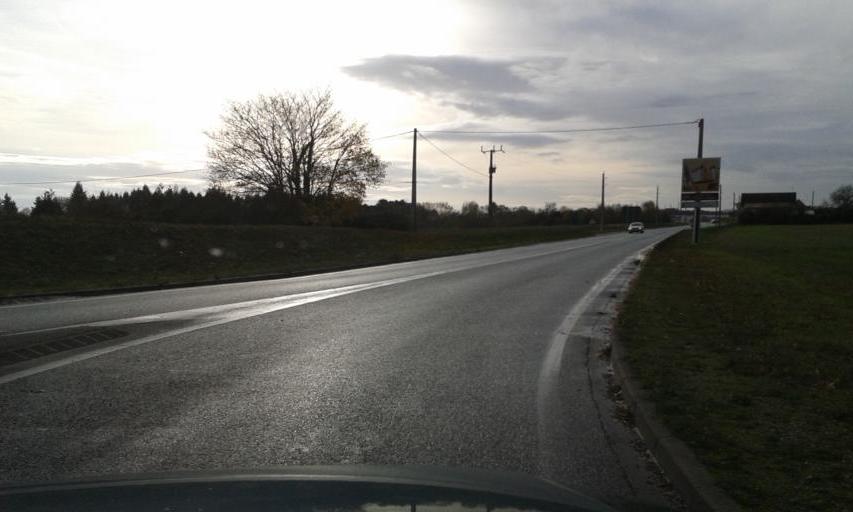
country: FR
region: Centre
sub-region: Departement du Loiret
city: Saint-Ay
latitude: 47.8470
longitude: 1.7252
